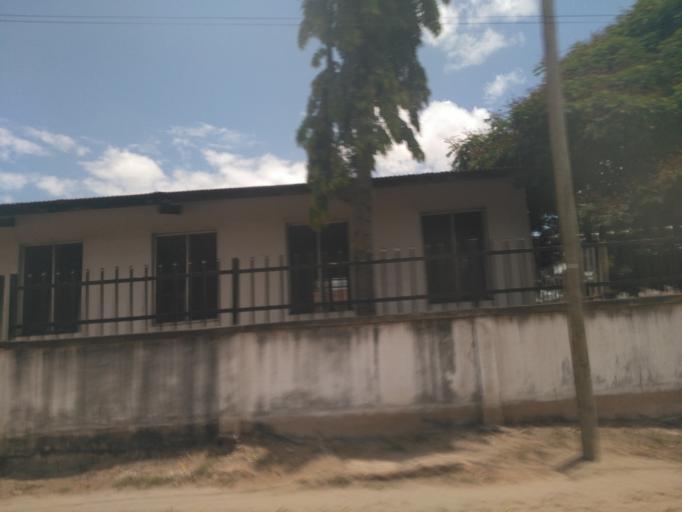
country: TZ
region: Dar es Salaam
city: Dar es Salaam
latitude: -6.8591
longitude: 39.2629
